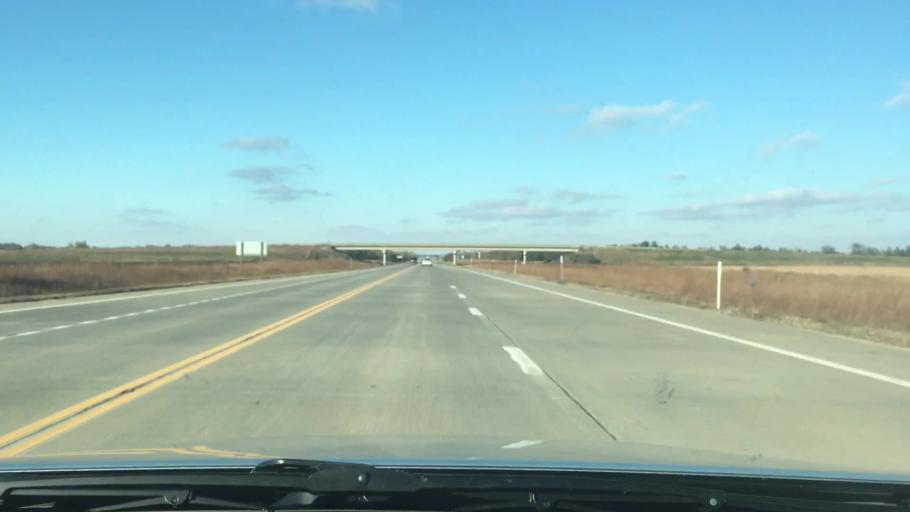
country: US
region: Kansas
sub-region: Reno County
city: South Hutchinson
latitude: 38.0396
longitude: -97.9857
